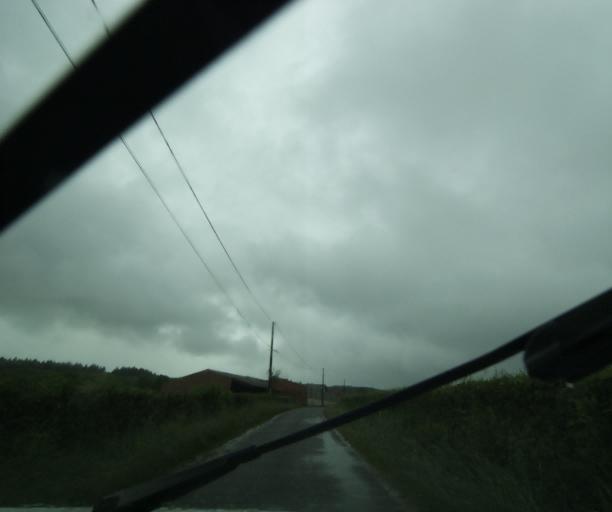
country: FR
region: Bourgogne
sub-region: Departement de Saone-et-Loire
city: Palinges
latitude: 46.5262
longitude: 4.2941
